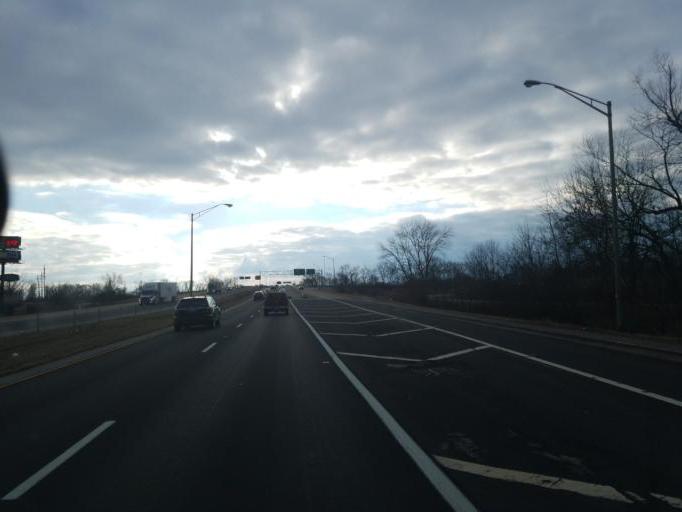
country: US
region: Illinois
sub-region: Madison County
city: Mitchell
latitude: 38.7619
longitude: -90.1011
